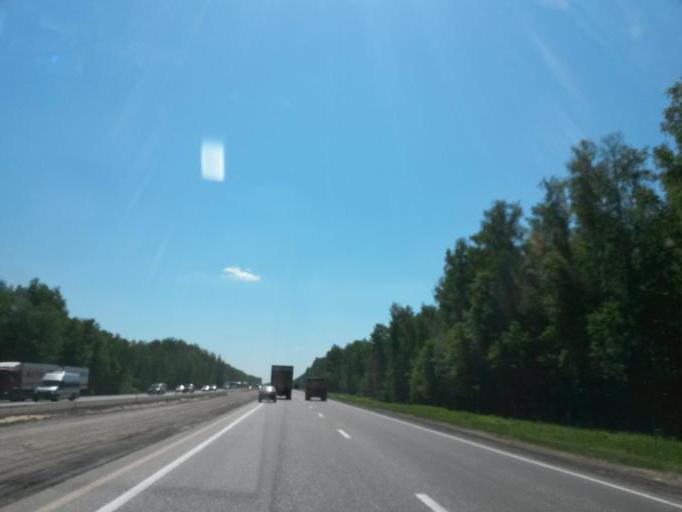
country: RU
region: Moskovskaya
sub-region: Chekhovskiy Rayon
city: Chekhov
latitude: 55.1724
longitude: 37.5386
